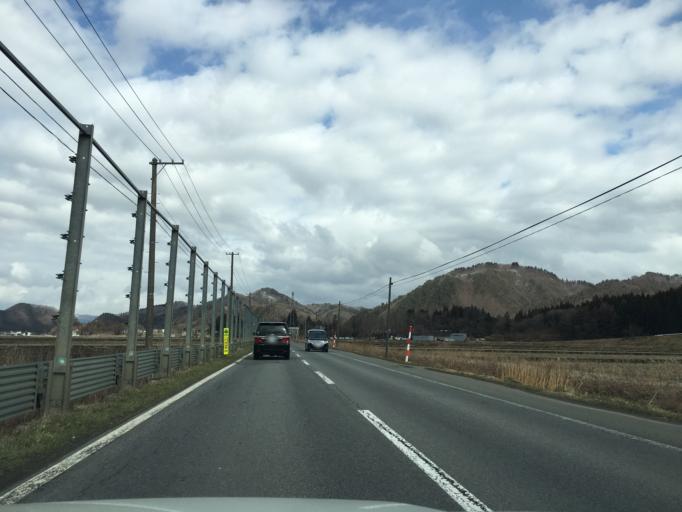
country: JP
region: Akita
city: Hanawa
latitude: 40.2261
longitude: 140.7264
